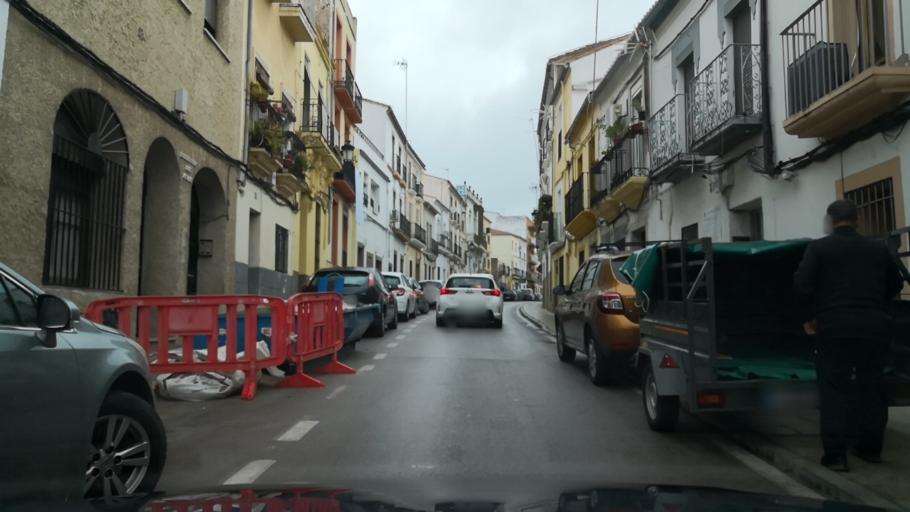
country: ES
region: Extremadura
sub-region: Provincia de Caceres
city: Caceres
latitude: 39.4771
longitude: -6.3725
